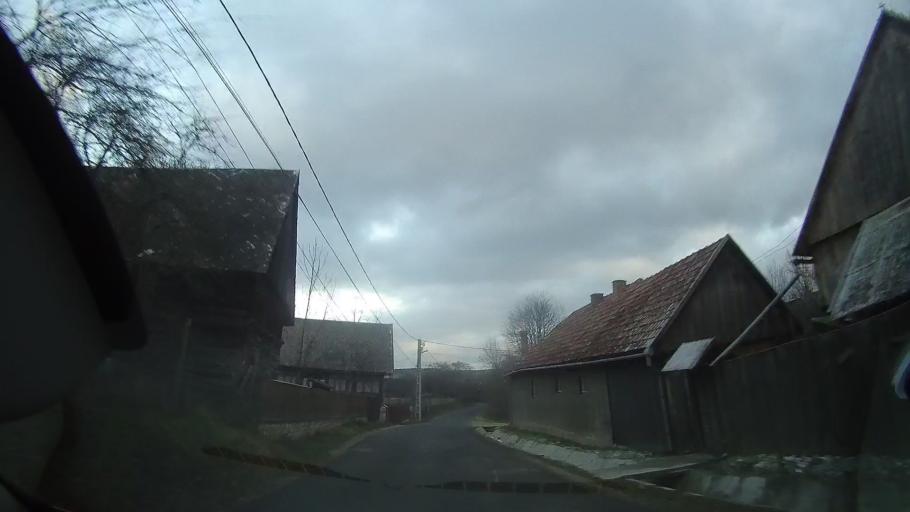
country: RO
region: Cluj
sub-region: Comuna Manastireni
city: Manastireni
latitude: 46.7815
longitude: 23.0740
